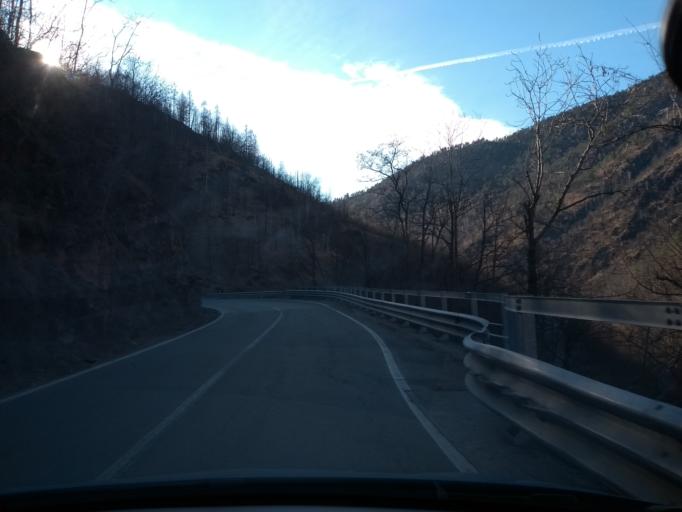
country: IT
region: Piedmont
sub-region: Provincia di Torino
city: La Villa
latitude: 45.2492
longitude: 7.4344
